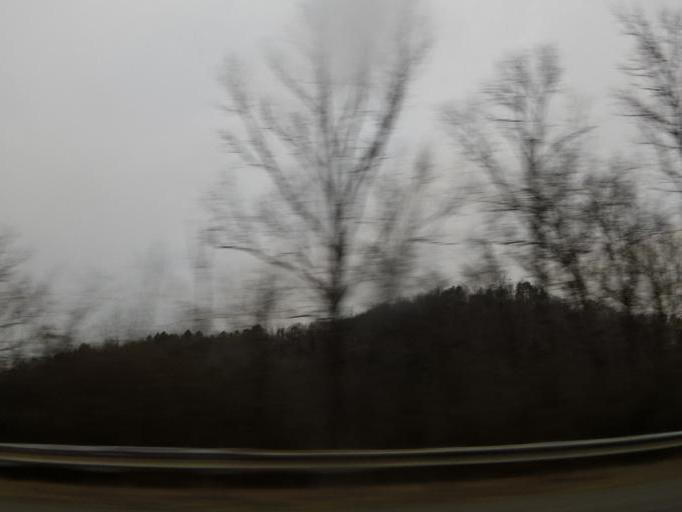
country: US
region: Alabama
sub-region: Cullman County
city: Good Hope
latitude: 34.0243
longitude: -86.8712
